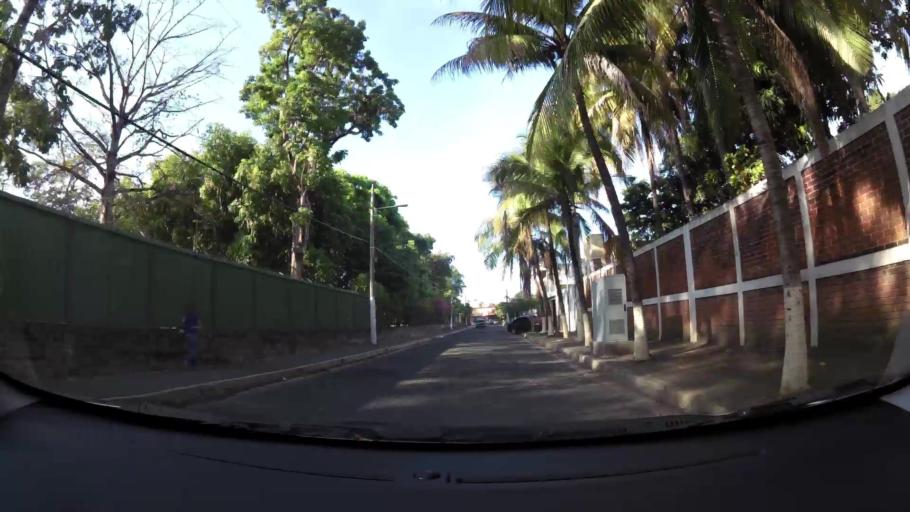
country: SV
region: San Miguel
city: San Miguel
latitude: 13.4725
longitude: -88.1875
